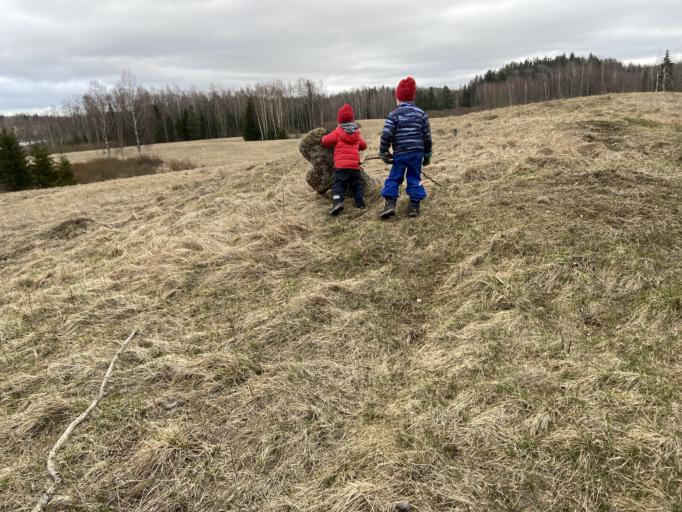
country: EE
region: Tartu
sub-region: Elva linn
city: Elva
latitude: 58.0573
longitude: 26.5064
